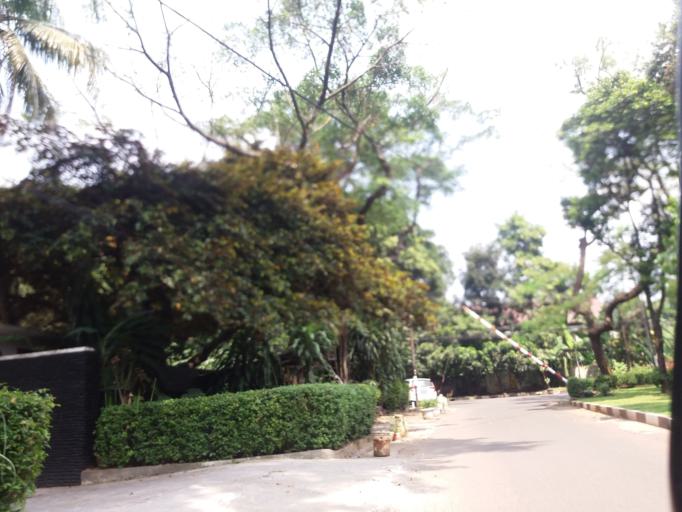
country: ID
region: Jakarta Raya
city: Jakarta
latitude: -6.2322
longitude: 106.8051
